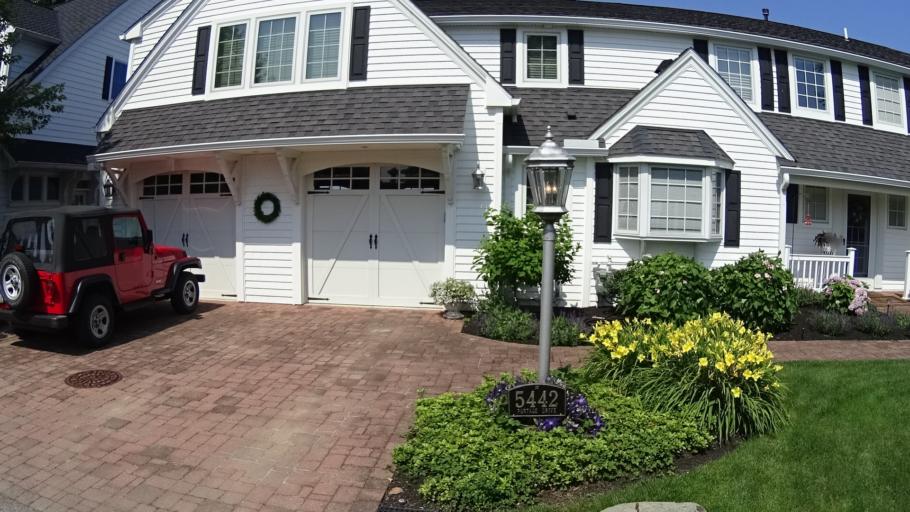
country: US
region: Ohio
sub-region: Lorain County
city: Vermilion
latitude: 41.4265
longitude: -82.3633
